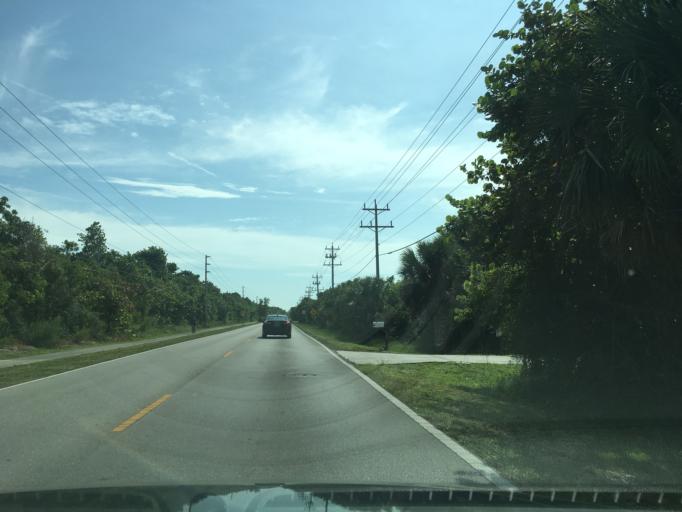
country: US
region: Florida
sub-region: Lee County
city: Saint James City
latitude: 26.4629
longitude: -82.1490
